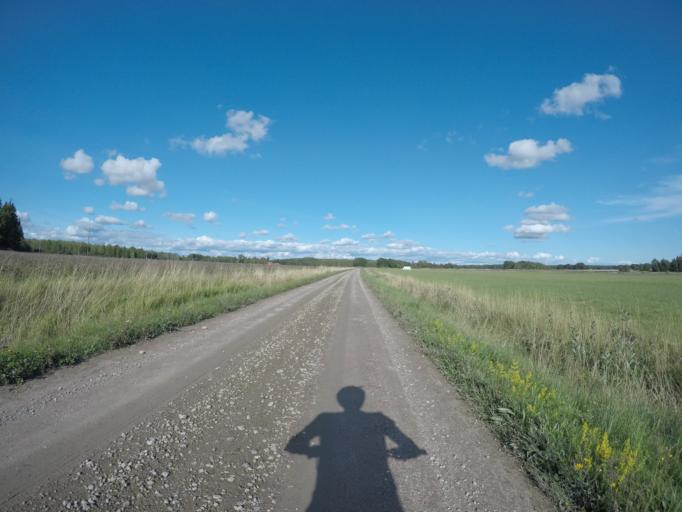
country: SE
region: Soedermanland
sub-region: Eskilstuna Kommun
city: Kvicksund
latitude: 59.5060
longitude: 16.3382
